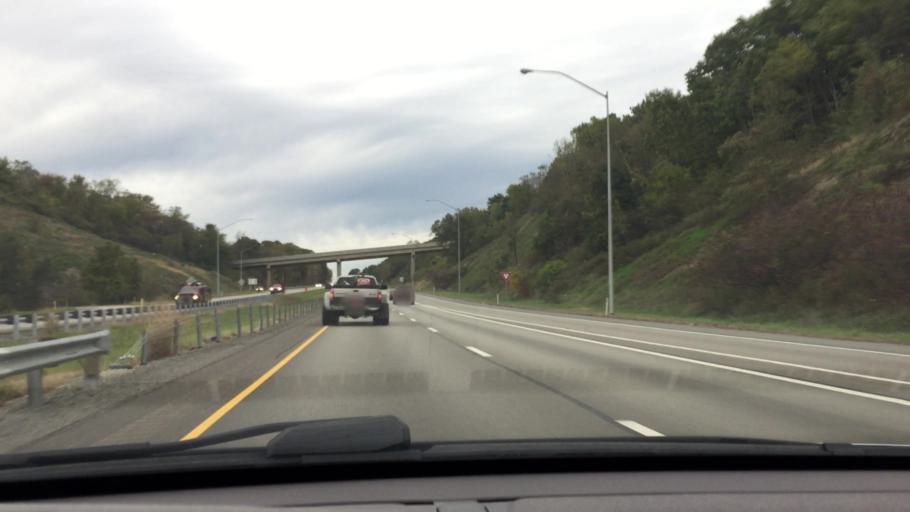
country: US
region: Pennsylvania
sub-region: Beaver County
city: Ambridge
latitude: 40.5593
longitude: -80.2795
